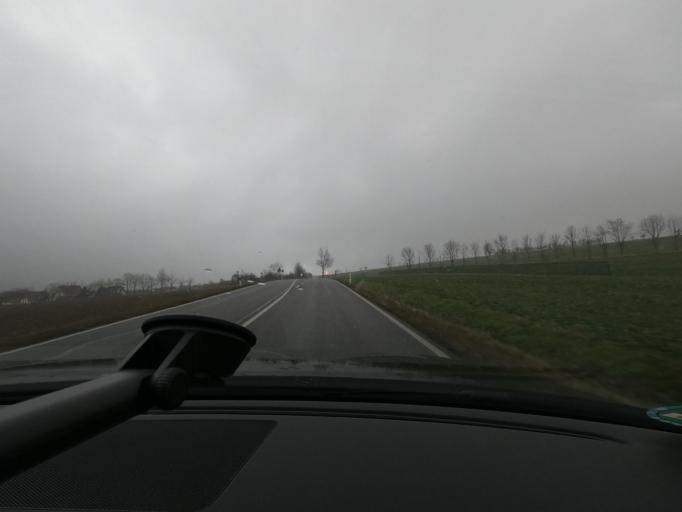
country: DE
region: Thuringia
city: Helmsdorf
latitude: 51.2953
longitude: 10.3422
